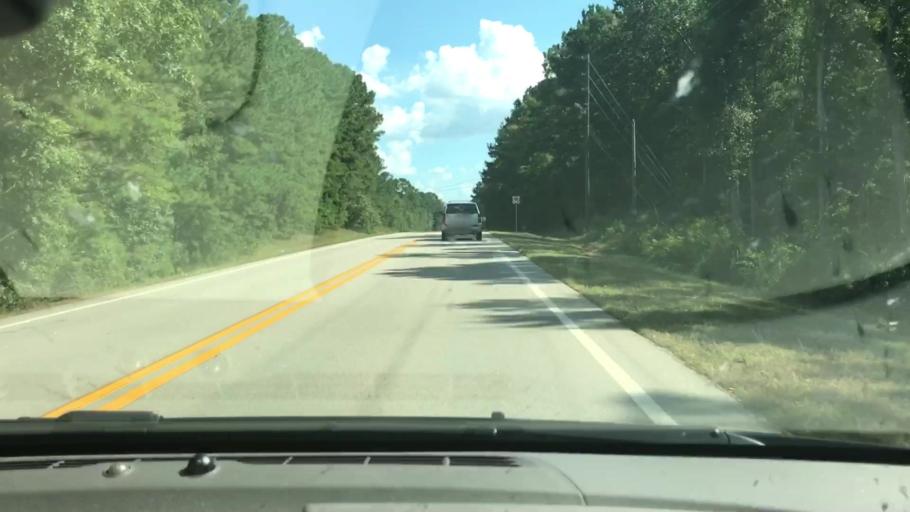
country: US
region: Georgia
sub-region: Troup County
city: La Grange
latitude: 33.0939
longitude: -85.0592
